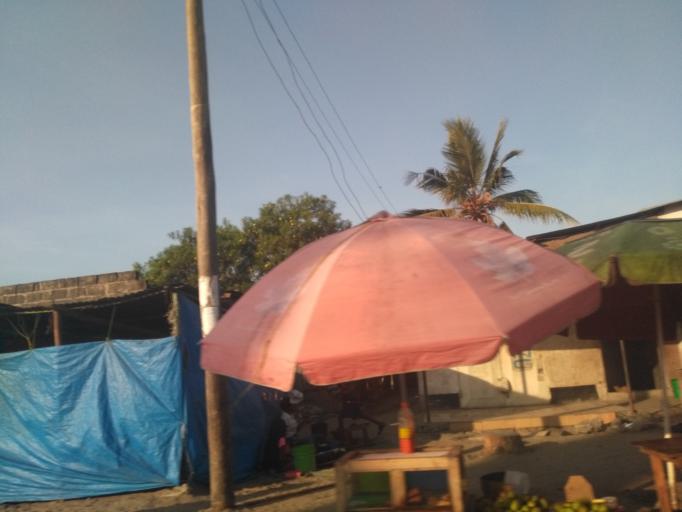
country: TZ
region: Dar es Salaam
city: Dar es Salaam
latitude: -6.9032
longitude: 39.2678
